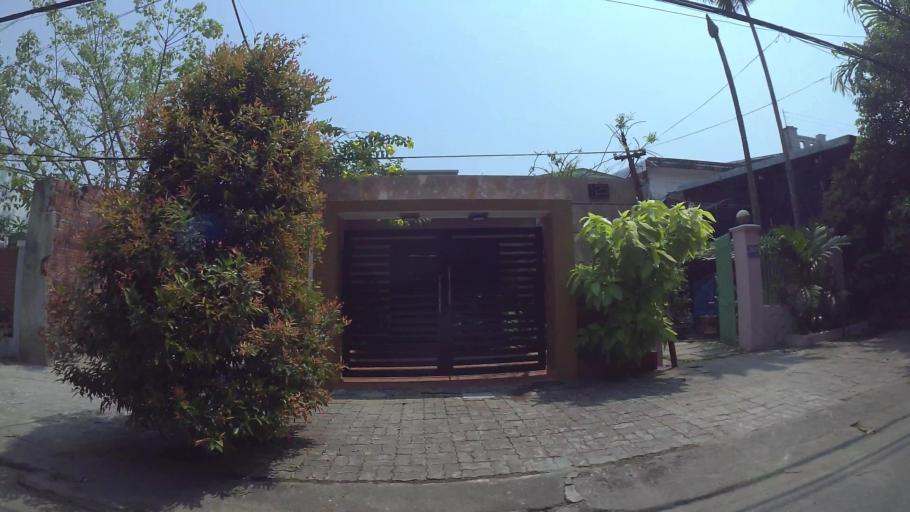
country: VN
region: Da Nang
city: Cam Le
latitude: 15.9885
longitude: 108.2066
